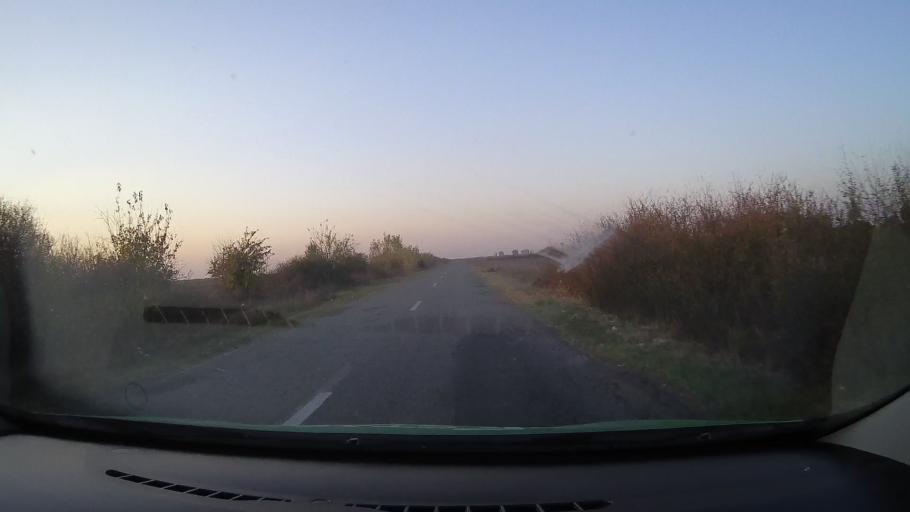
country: RO
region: Arad
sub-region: Comuna Zarand
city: Zarand
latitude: 46.3816
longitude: 21.6670
